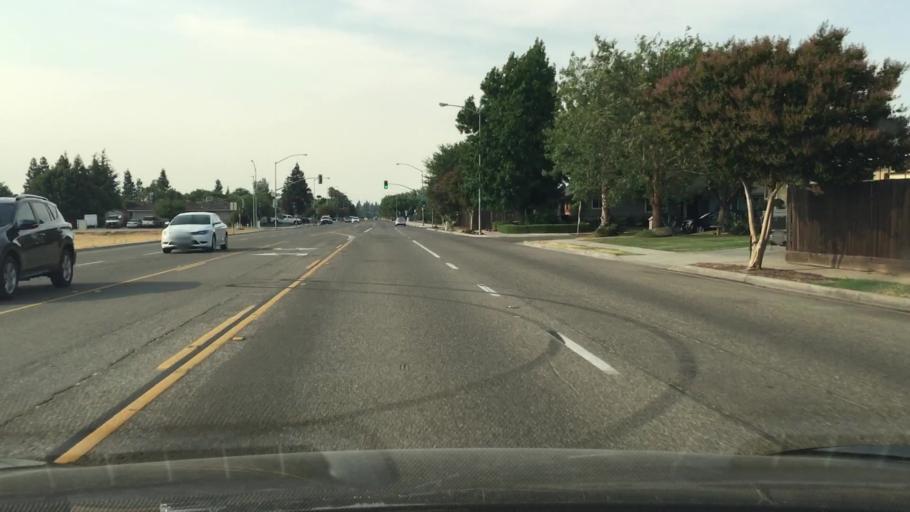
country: US
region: California
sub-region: Fresno County
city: Clovis
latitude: 36.8291
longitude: -119.7361
